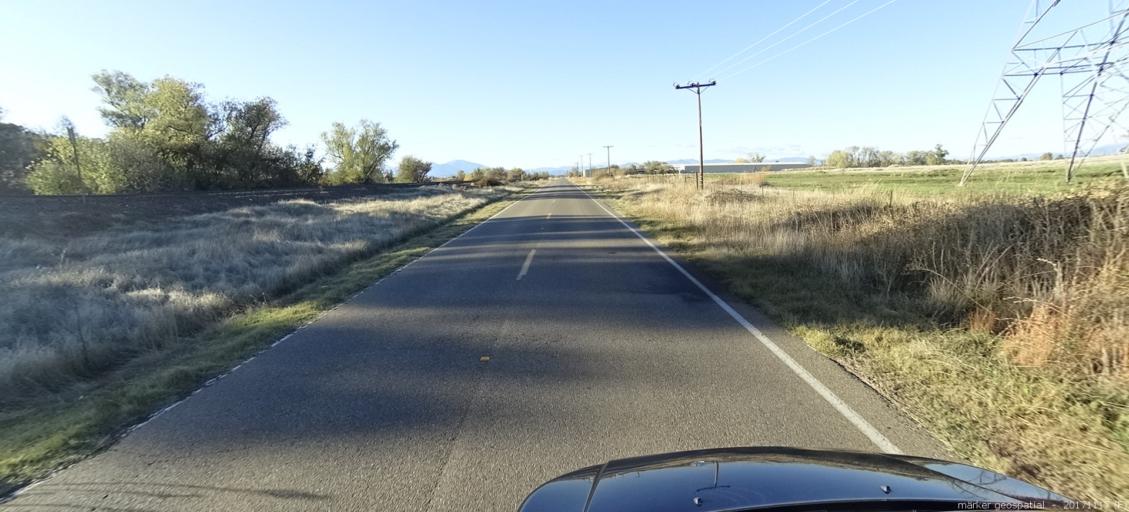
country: US
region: California
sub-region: Shasta County
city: Cottonwood
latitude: 40.4168
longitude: -122.2514
